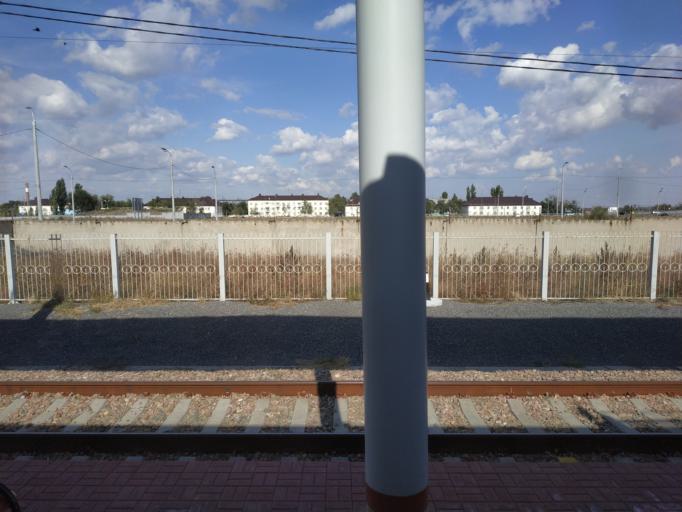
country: RU
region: Volgograd
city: Gumrak
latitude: 48.7930
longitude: 44.3590
